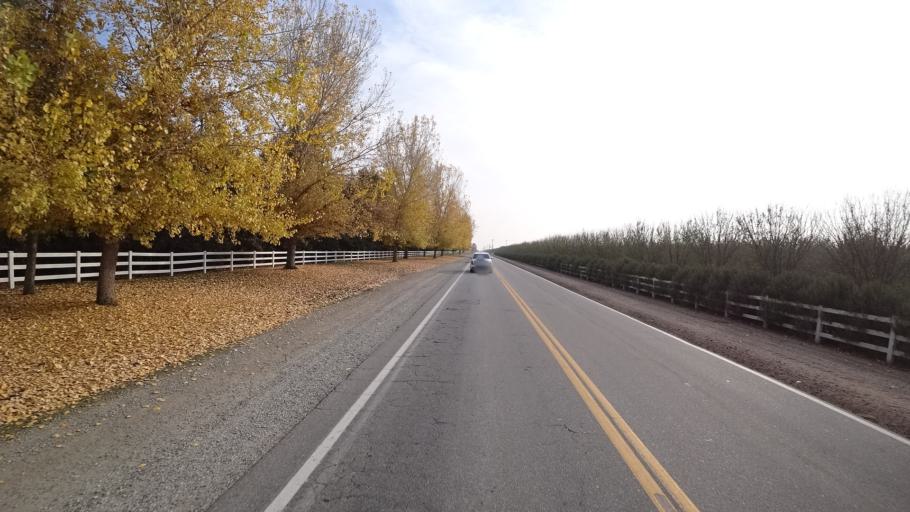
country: US
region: California
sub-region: Kern County
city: Greenacres
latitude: 35.2915
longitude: -119.1282
